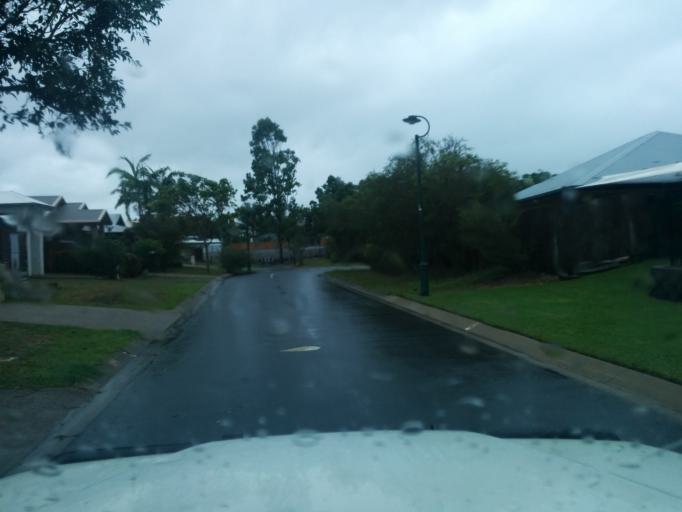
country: AU
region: Queensland
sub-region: Cairns
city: Woree
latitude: -16.9862
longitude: 145.7376
